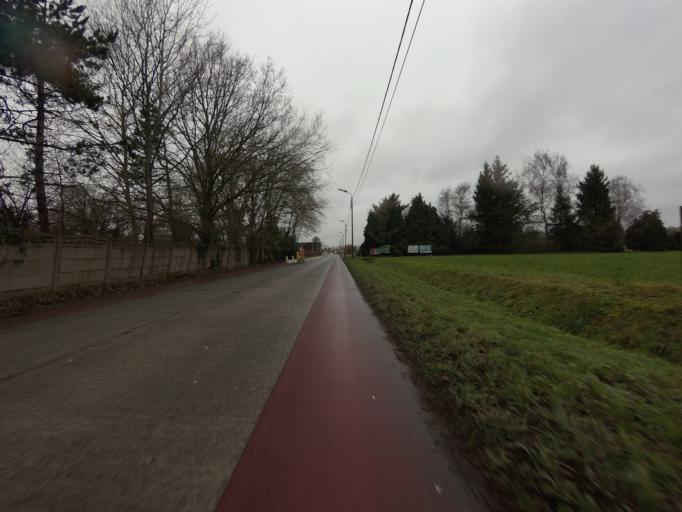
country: BE
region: Flanders
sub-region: Provincie Antwerpen
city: Sint-Katelijne-Waver
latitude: 51.0519
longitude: 4.5367
